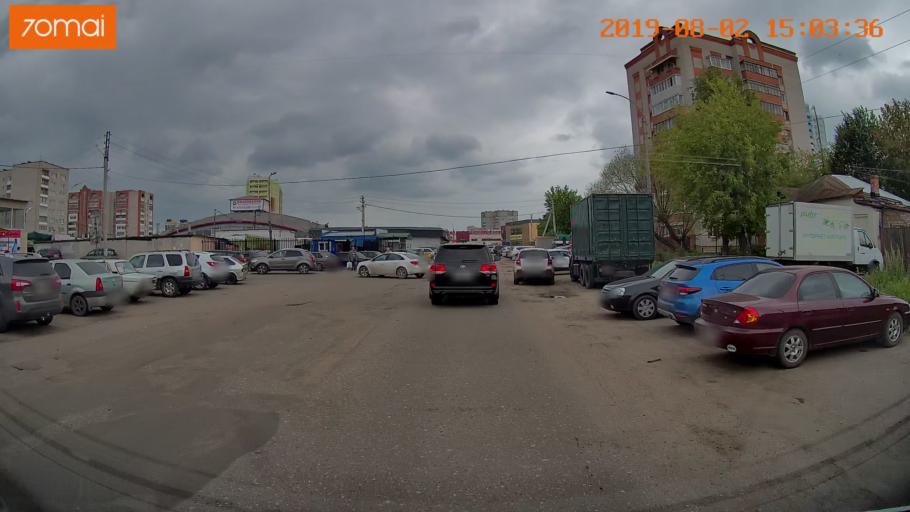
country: RU
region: Ivanovo
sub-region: Gorod Ivanovo
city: Ivanovo
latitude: 56.9900
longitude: 40.9660
